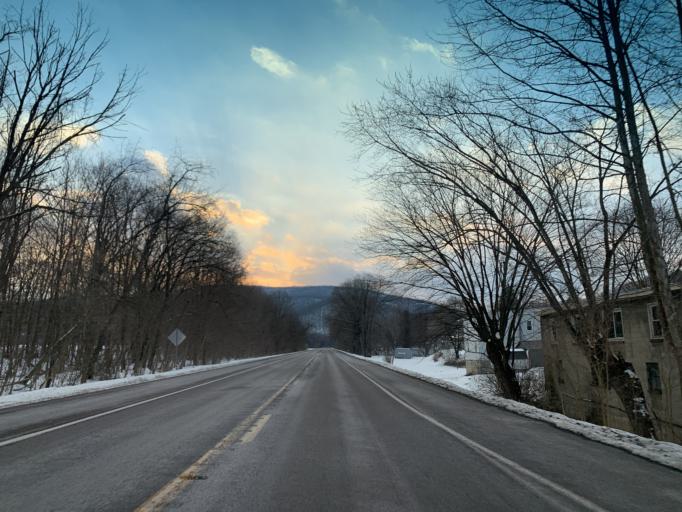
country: US
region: Maryland
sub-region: Allegany County
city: La Vale
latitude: 39.6928
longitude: -78.7919
